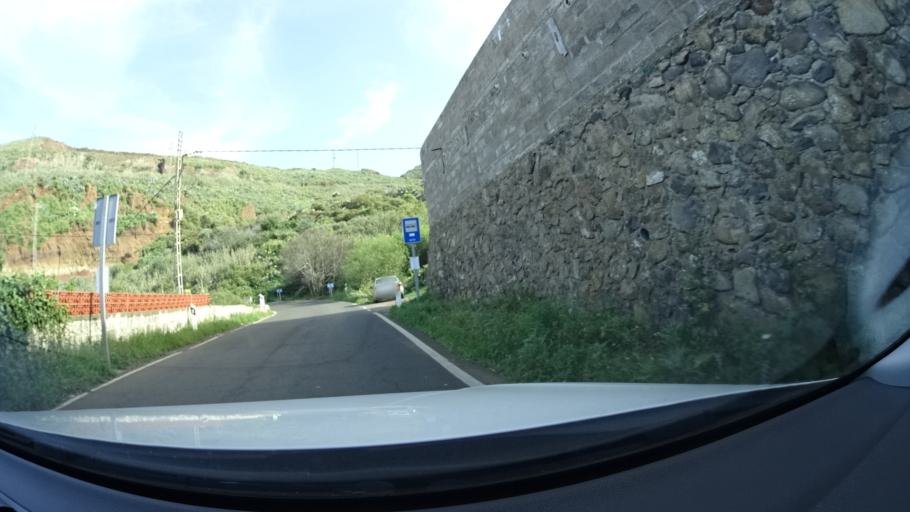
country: ES
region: Canary Islands
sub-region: Provincia de Las Palmas
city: Guia
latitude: 28.1082
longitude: -15.6411
